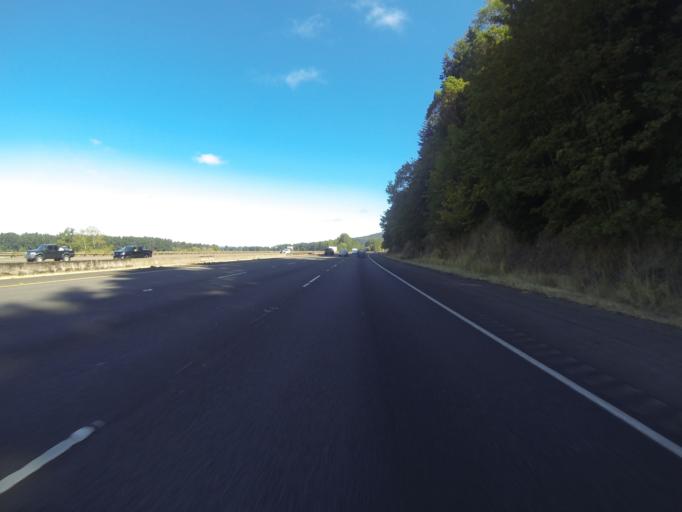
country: US
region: Washington
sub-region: Cowlitz County
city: Kalama
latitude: 46.0687
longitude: -122.8680
